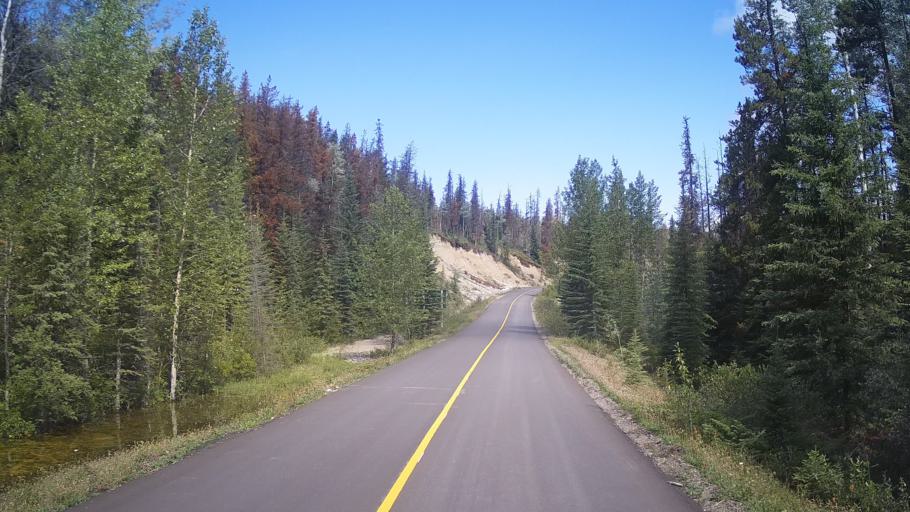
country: CA
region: Alberta
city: Jasper Park Lodge
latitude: 52.6658
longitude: -117.8893
